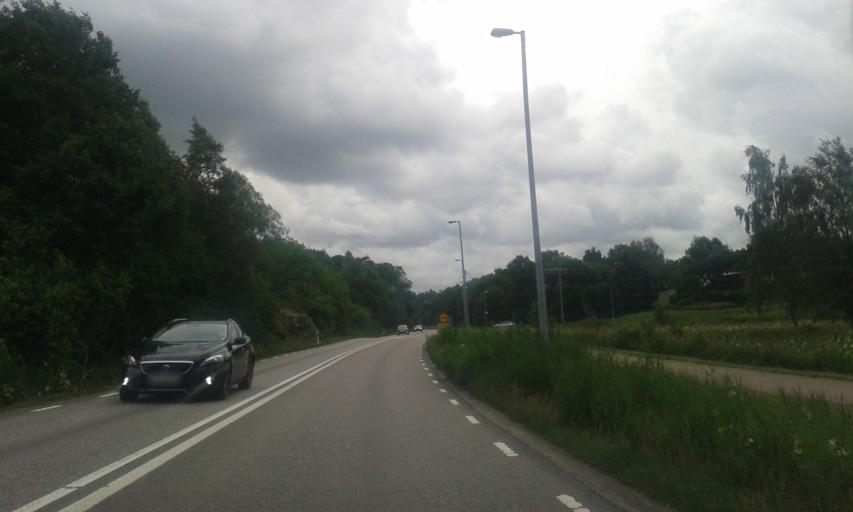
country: SE
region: Vaestra Goetaland
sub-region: Kungalvs Kommun
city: Kungalv
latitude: 57.8706
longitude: 11.9114
